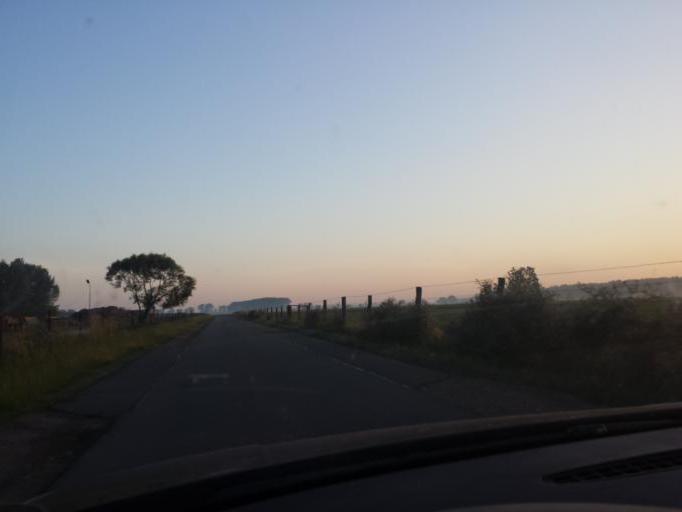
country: DE
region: Brandenburg
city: Kremmen
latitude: 52.8167
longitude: 13.0013
